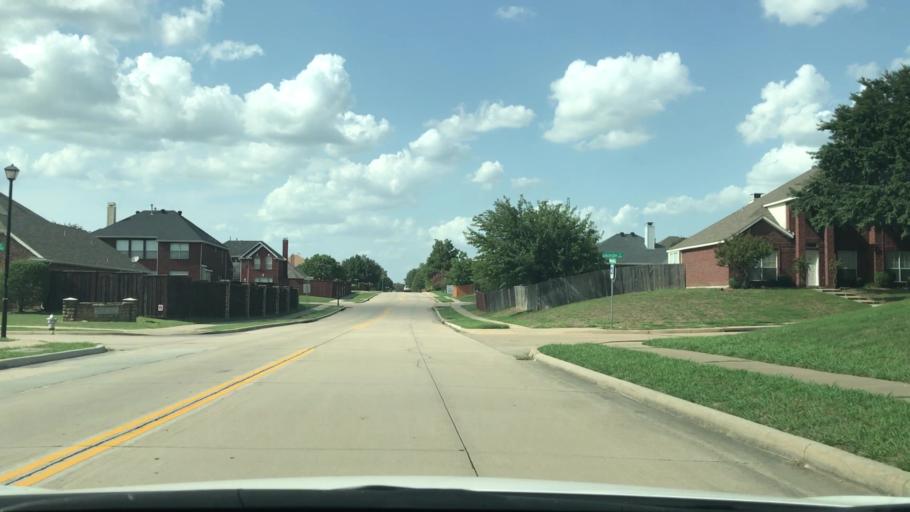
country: US
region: Texas
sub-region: Dallas County
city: Carrollton
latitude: 32.9768
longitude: -96.8643
